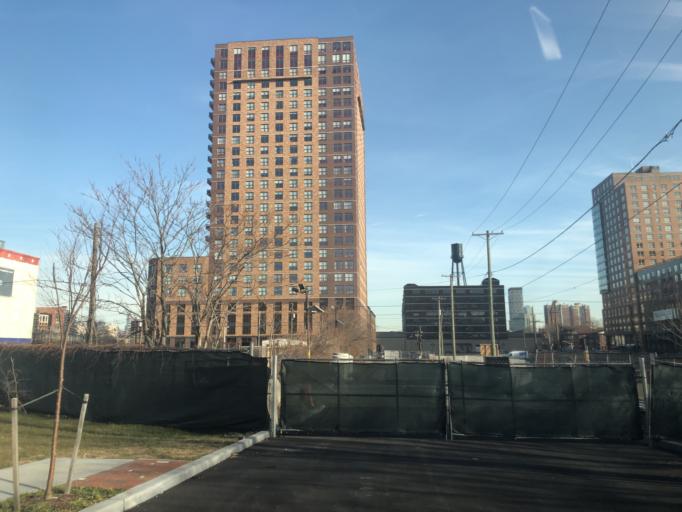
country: US
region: New Jersey
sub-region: Hudson County
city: Hoboken
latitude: 40.7343
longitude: -74.0474
